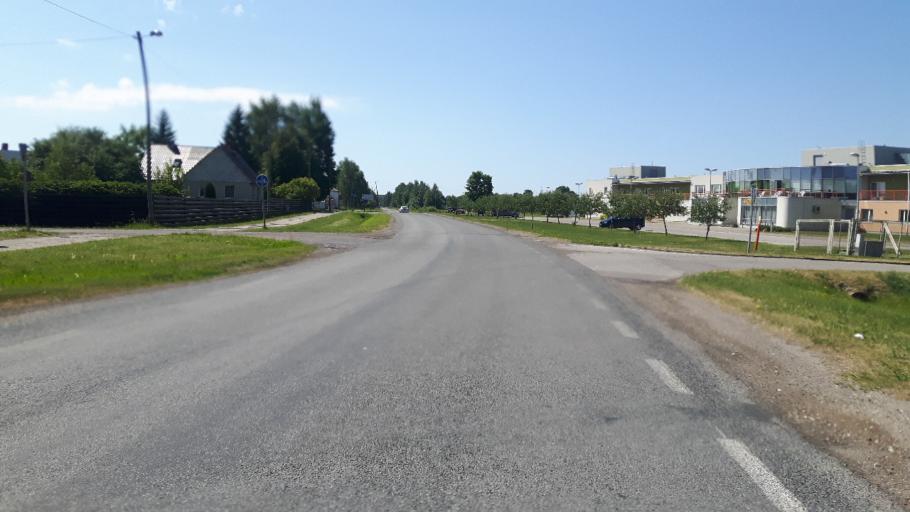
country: EE
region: Paernumaa
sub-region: Vaendra vald (alev)
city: Vandra
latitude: 58.6465
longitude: 25.0293
